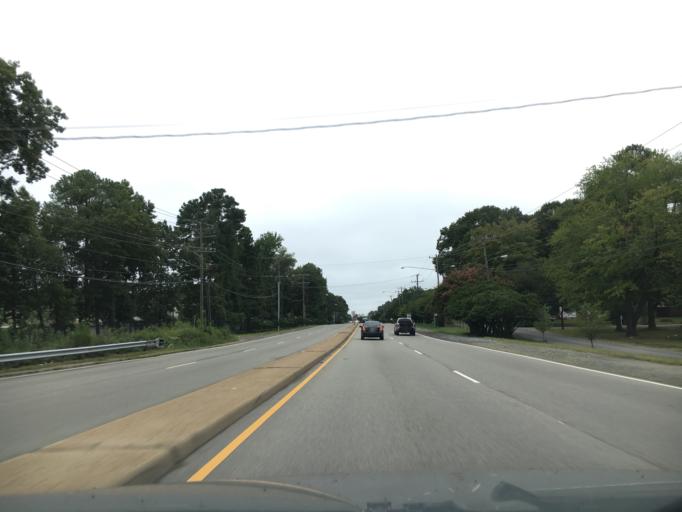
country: US
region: Virginia
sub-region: City of Richmond
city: Richmond
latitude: 37.4979
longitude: -77.4802
